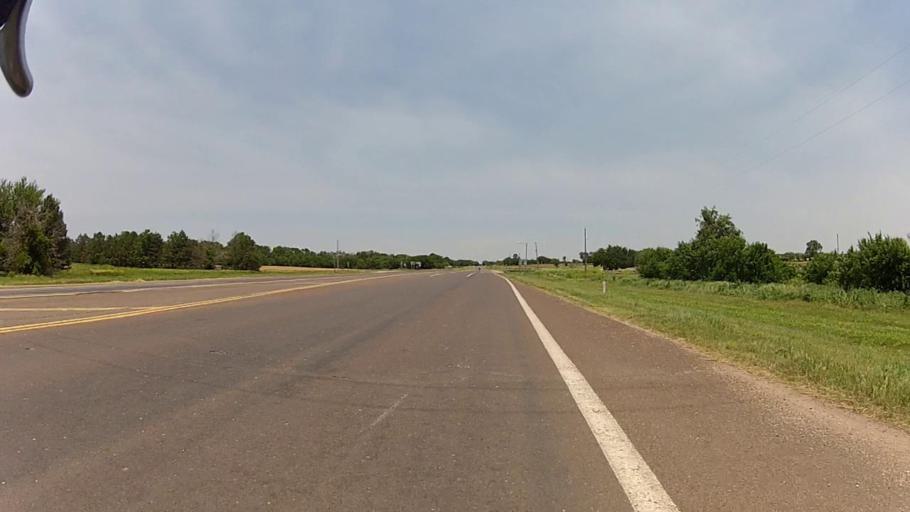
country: US
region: Kansas
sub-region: Sumner County
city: Caldwell
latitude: 37.0556
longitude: -97.4012
